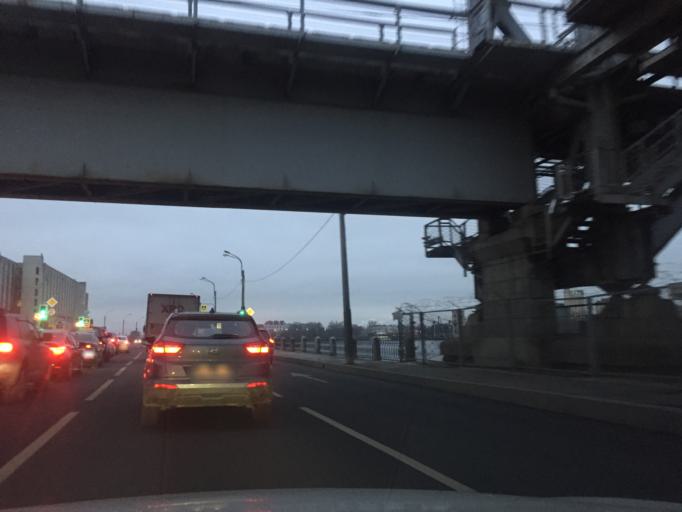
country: RU
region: St.-Petersburg
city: Centralniy
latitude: 59.9166
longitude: 30.4130
